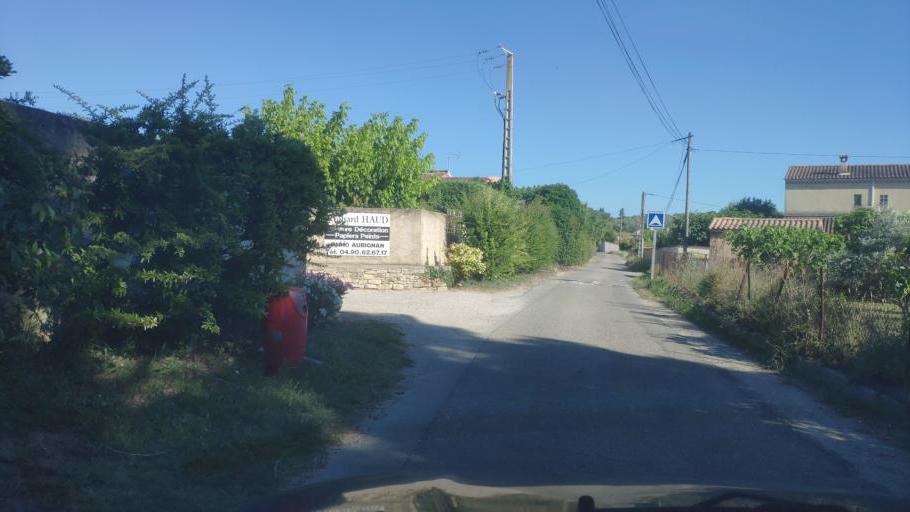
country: FR
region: Provence-Alpes-Cote d'Azur
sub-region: Departement du Vaucluse
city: Aubignan
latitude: 44.0914
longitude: 5.0358
